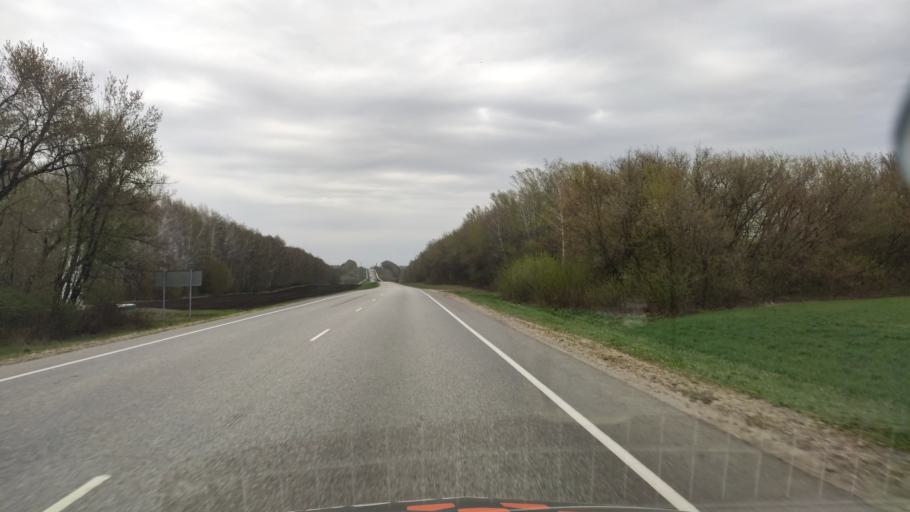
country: RU
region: Kursk
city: Olym
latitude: 51.5534
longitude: 38.2205
